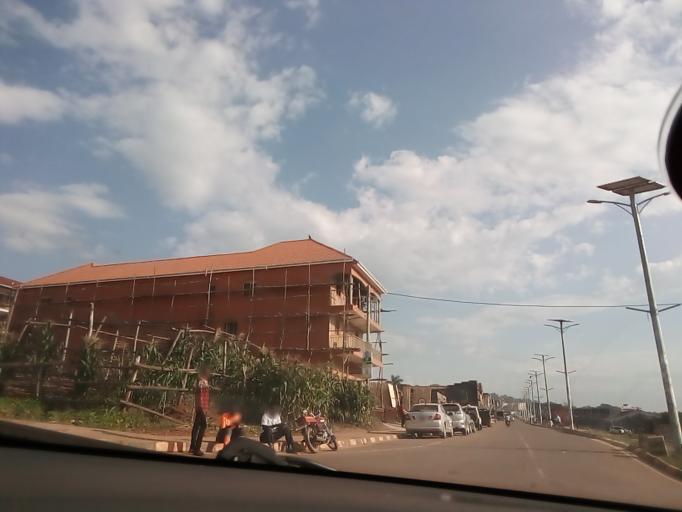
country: UG
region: Central Region
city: Masaka
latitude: -0.3472
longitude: 31.7412
